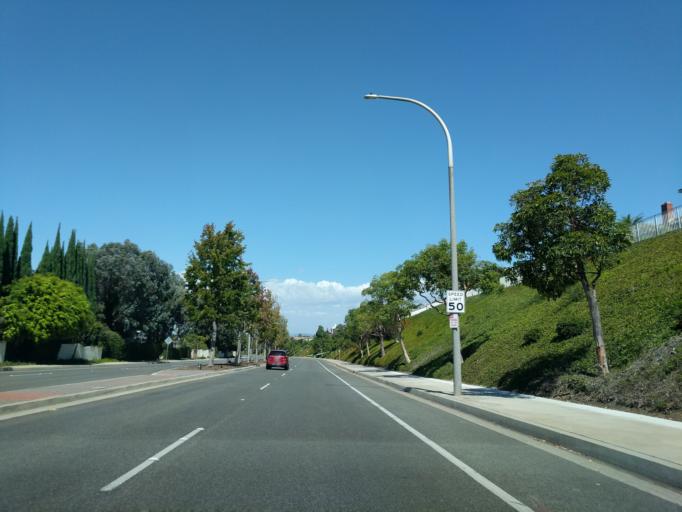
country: US
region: California
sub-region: Orange County
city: San Joaquin Hills
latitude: 33.6213
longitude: -117.8515
